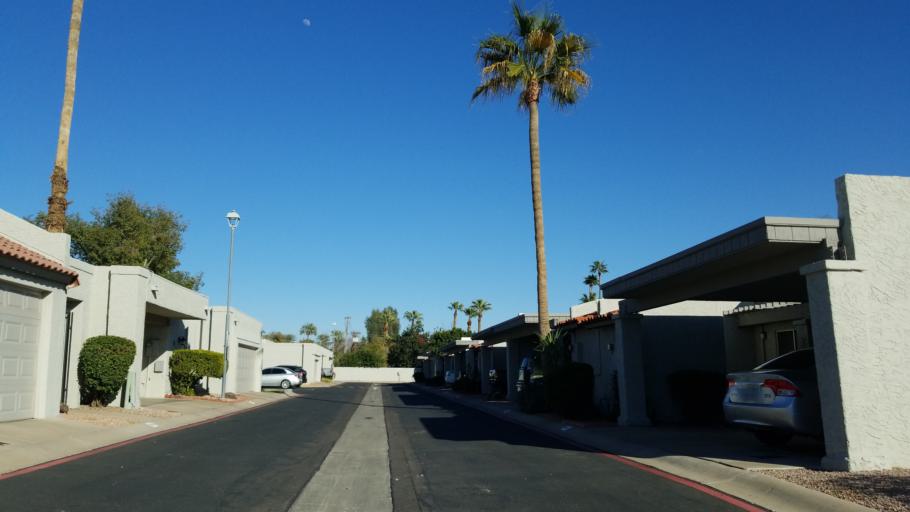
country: US
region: Arizona
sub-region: Maricopa County
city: Phoenix
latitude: 33.5114
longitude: -112.0628
